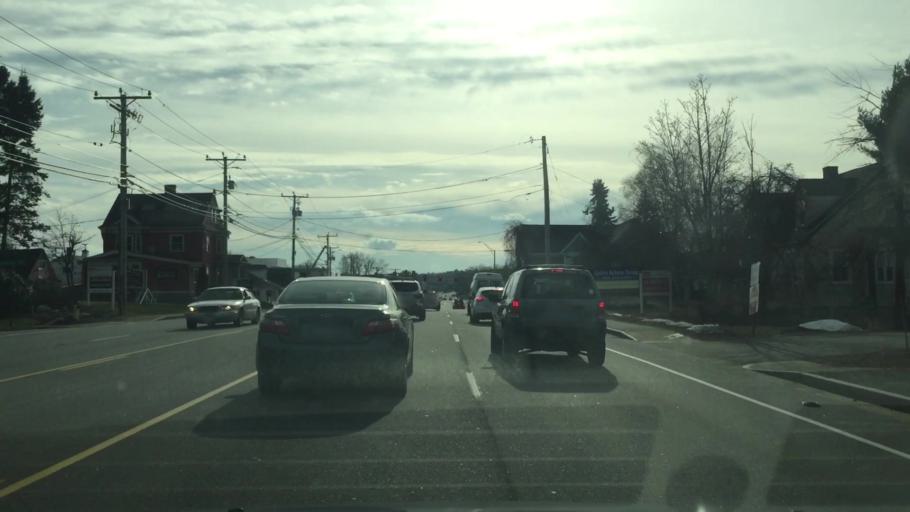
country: US
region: New Hampshire
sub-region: Hillsborough County
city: Bedford
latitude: 42.9627
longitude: -71.4801
